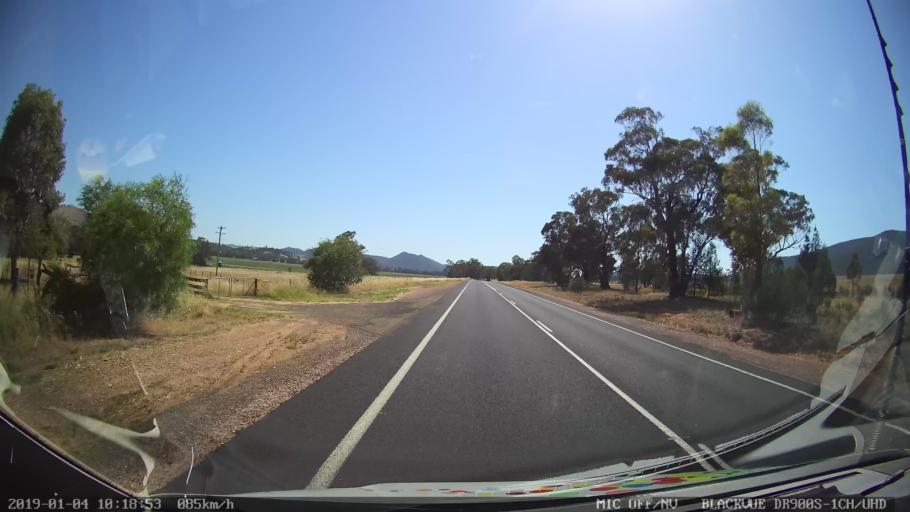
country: AU
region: New South Wales
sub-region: Cabonne
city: Canowindra
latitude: -33.3796
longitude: 148.4729
